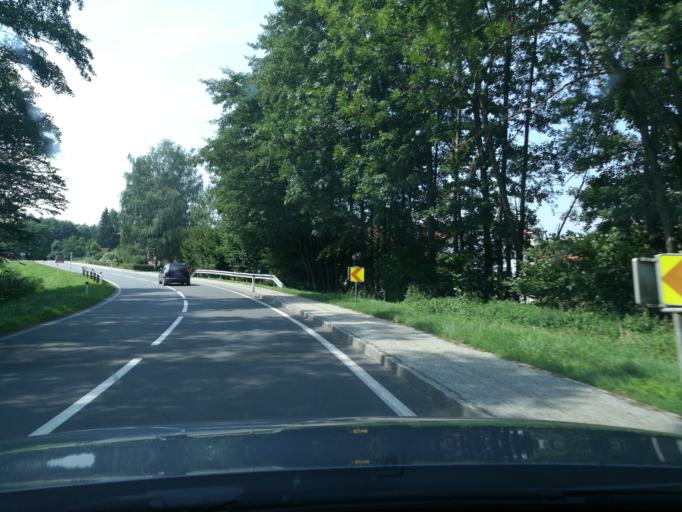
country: AT
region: Upper Austria
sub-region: Politischer Bezirk Grieskirchen
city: Grieskirchen
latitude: 48.3490
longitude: 13.7518
